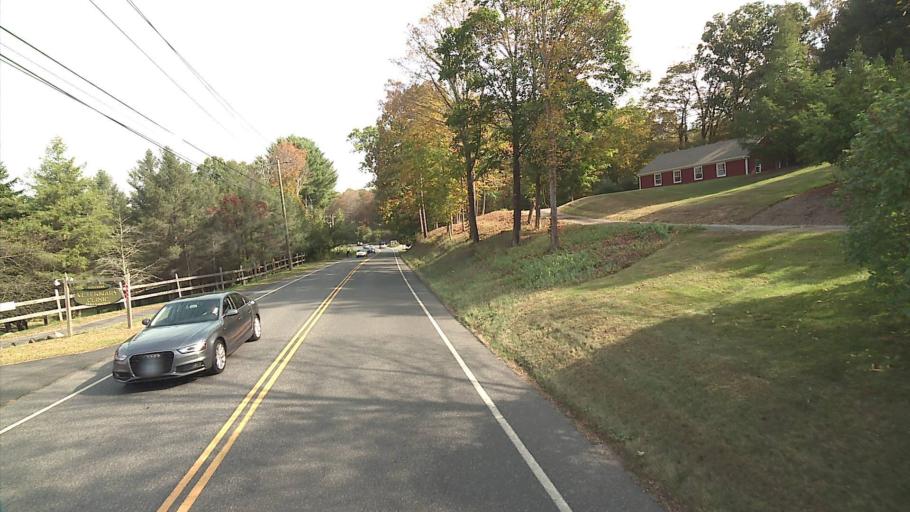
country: US
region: Connecticut
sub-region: New Haven County
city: Southbury
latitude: 41.5099
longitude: -73.2057
